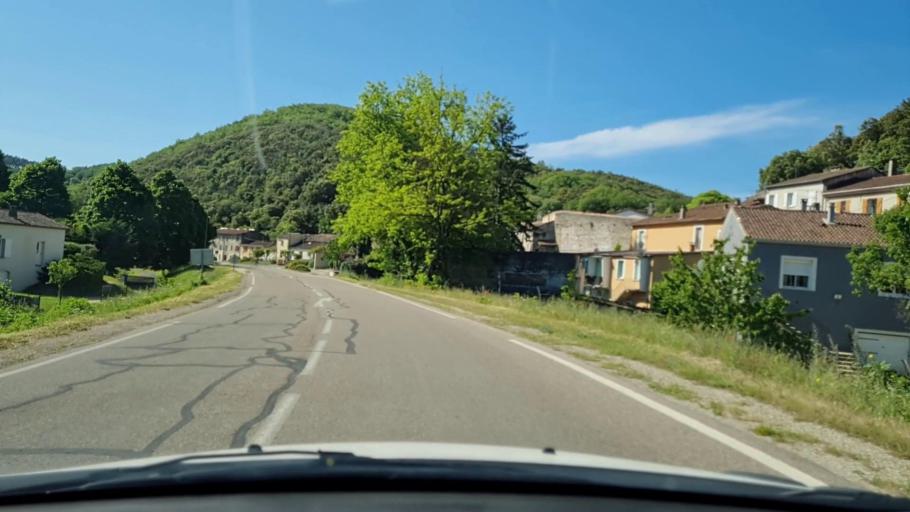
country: FR
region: Languedoc-Roussillon
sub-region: Departement du Gard
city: Cendras
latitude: 44.1492
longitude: 4.0573
